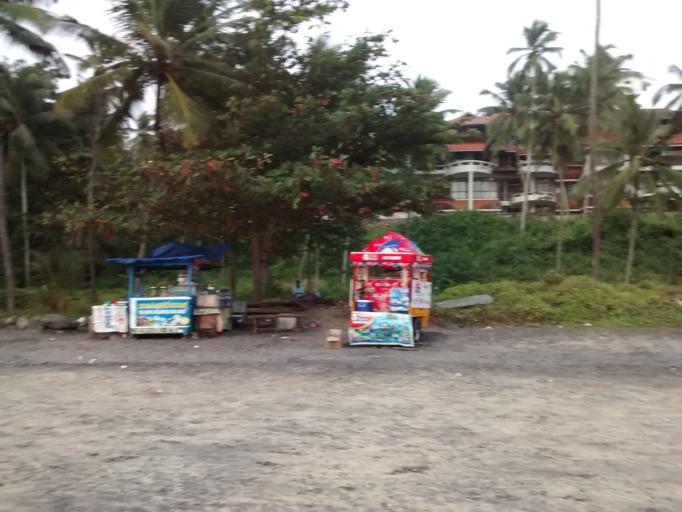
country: IN
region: Kerala
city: Kovalam
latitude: 8.3896
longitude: 76.9755
